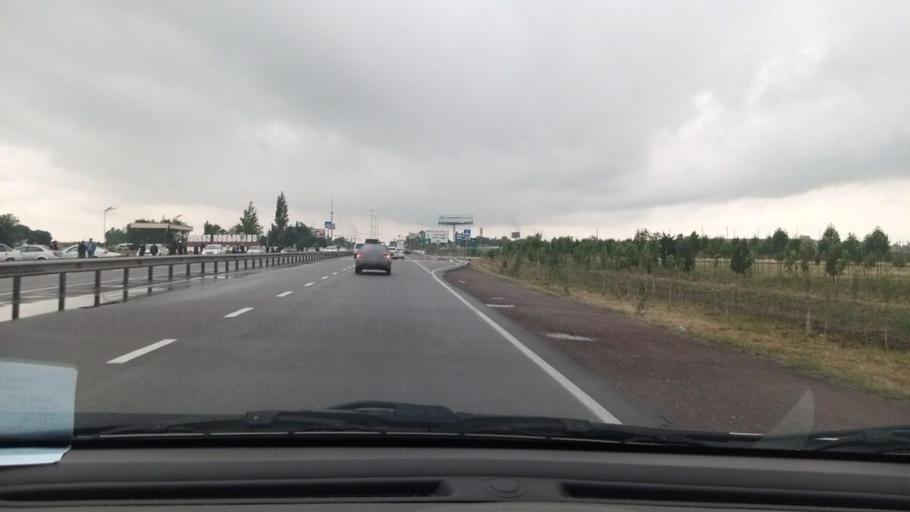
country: UZ
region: Toshkent
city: Ohangaron
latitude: 40.9188
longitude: 69.6005
